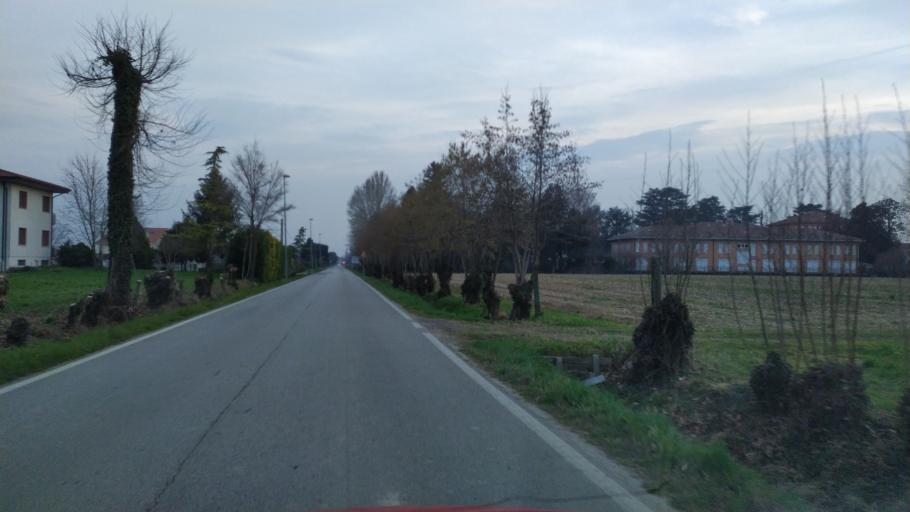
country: IT
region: Veneto
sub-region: Provincia di Vicenza
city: Vigardolo
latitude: 45.6124
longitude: 11.5867
